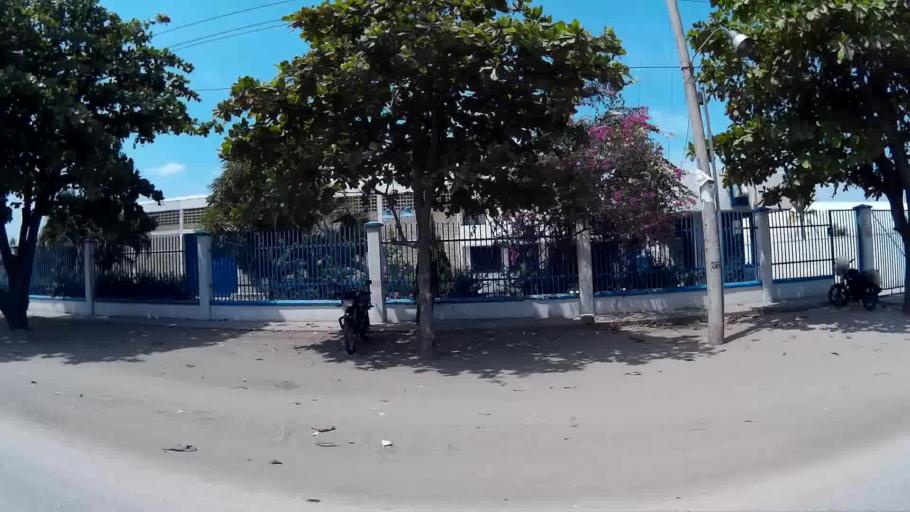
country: CO
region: Magdalena
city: Cienaga
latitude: 11.0050
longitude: -74.2364
